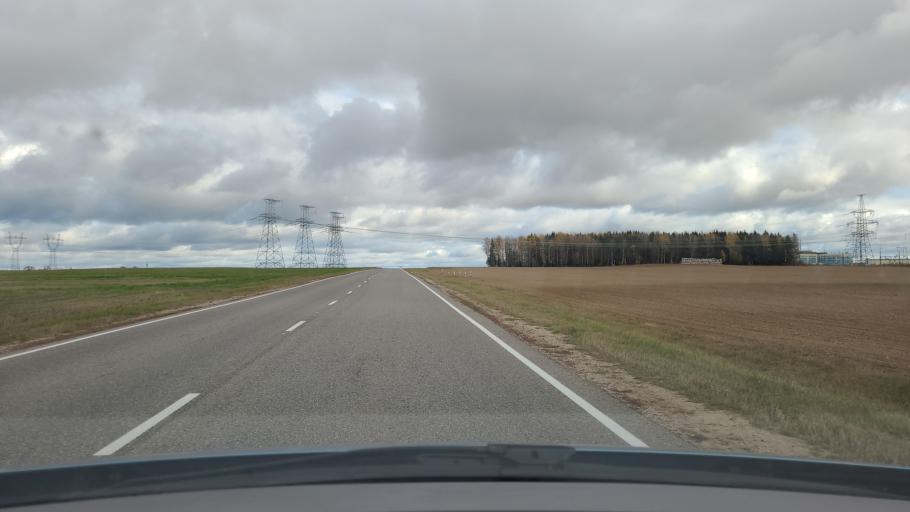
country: BY
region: Grodnenskaya
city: Astravyets
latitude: 54.7652
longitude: 26.0722
